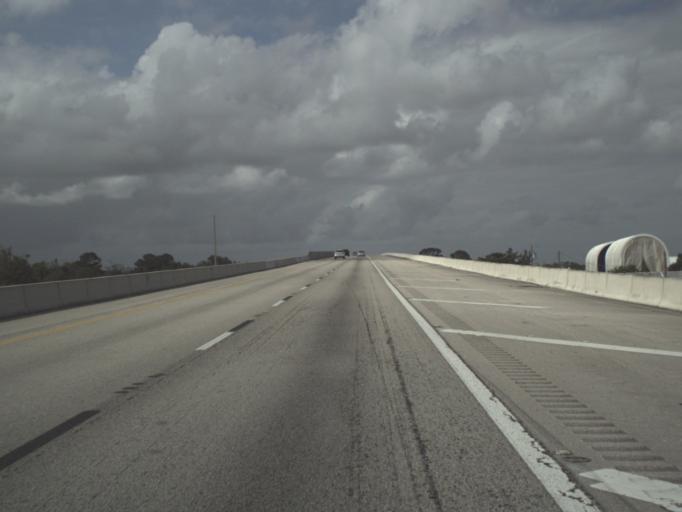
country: US
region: Florida
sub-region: Martin County
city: Palm City
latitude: 27.1126
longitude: -80.2713
